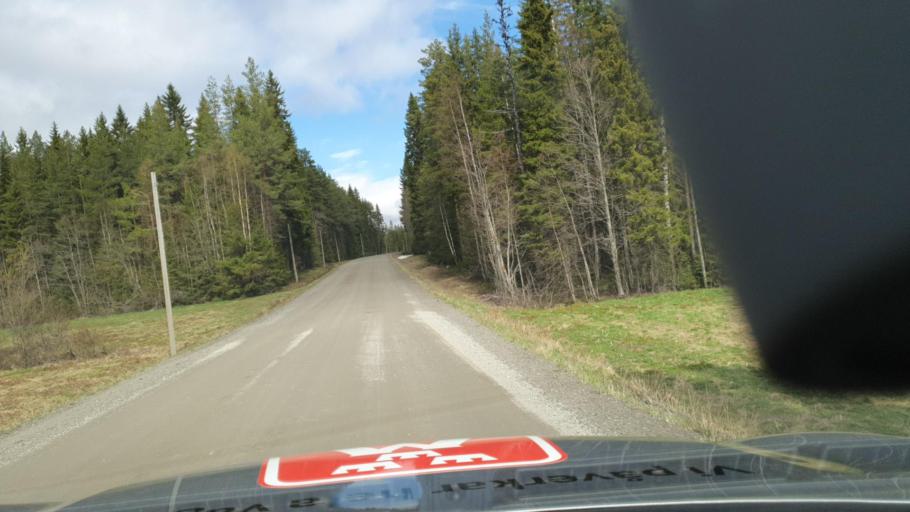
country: SE
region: Vaesterbotten
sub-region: Bjurholms Kommun
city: Bjurholm
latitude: 63.6994
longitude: 18.8973
